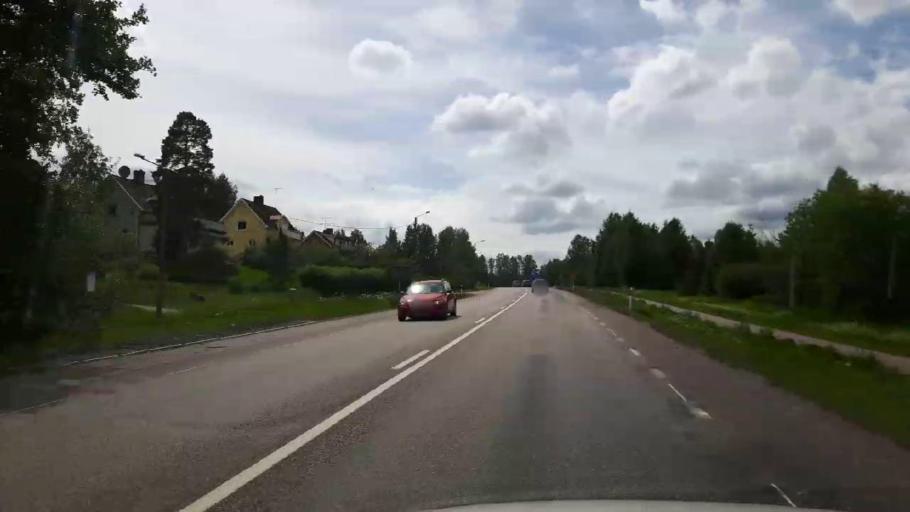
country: SE
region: Vaestmanland
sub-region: Fagersta Kommun
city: Fagersta
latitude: 59.9677
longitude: 15.7706
